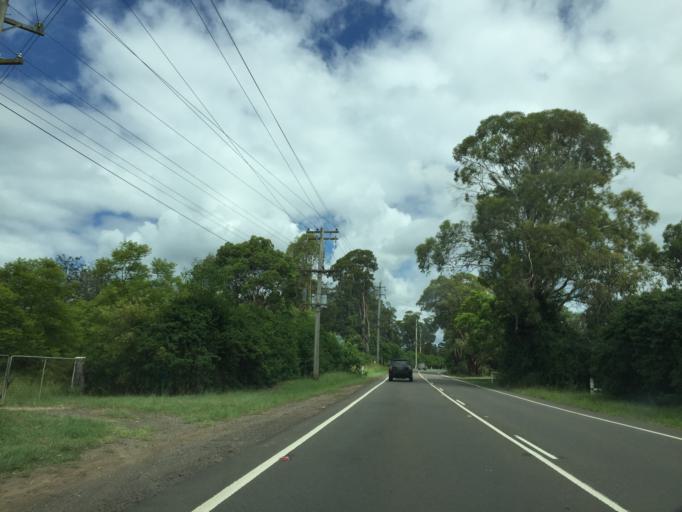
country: AU
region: New South Wales
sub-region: Hawkesbury
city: Richmond
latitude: -33.5507
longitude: 150.6863
